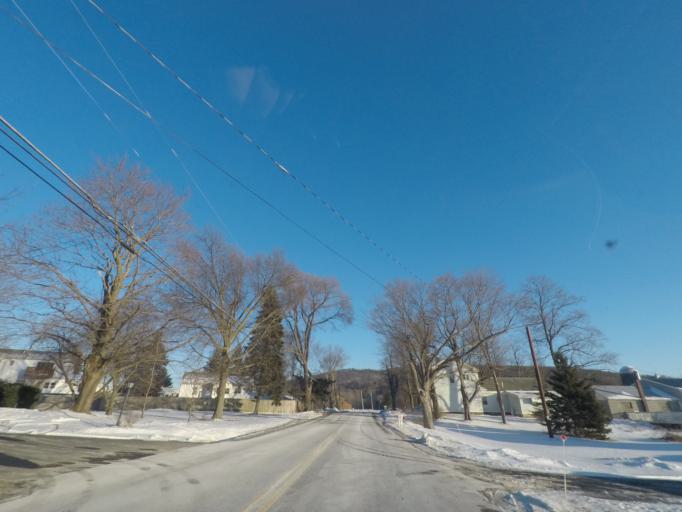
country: US
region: New York
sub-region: Saratoga County
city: Waterford
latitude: 42.8278
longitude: -73.6341
